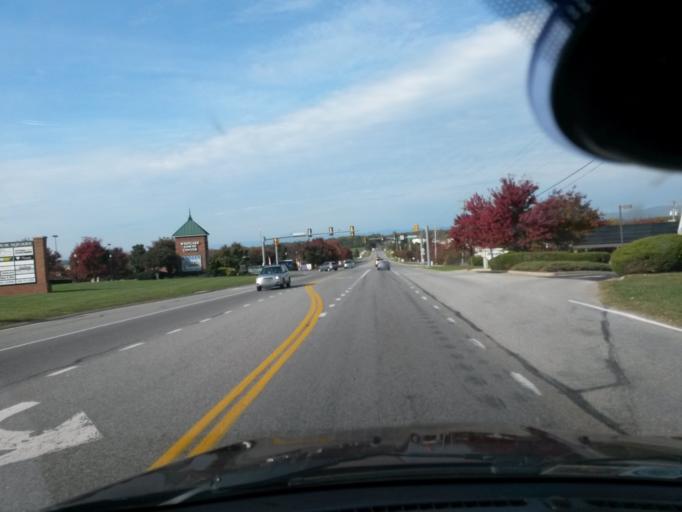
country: US
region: Virginia
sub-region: Franklin County
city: North Shore
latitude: 37.1196
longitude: -79.7172
